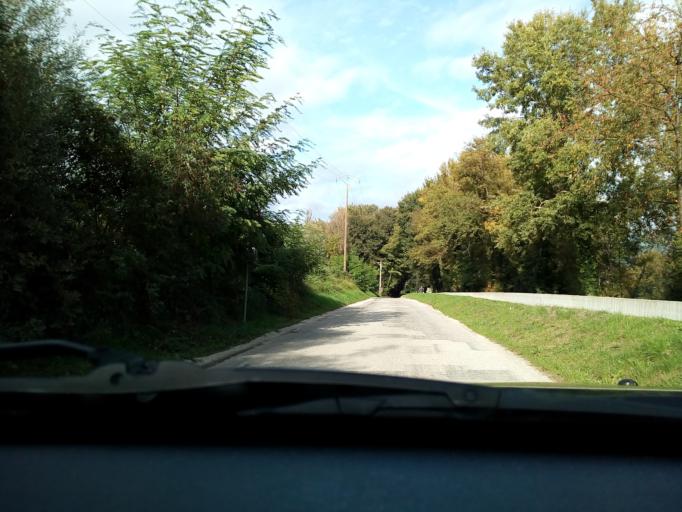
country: FR
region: Rhone-Alpes
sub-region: Departement de l'Isere
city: Domene
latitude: 45.2149
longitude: 5.8323
